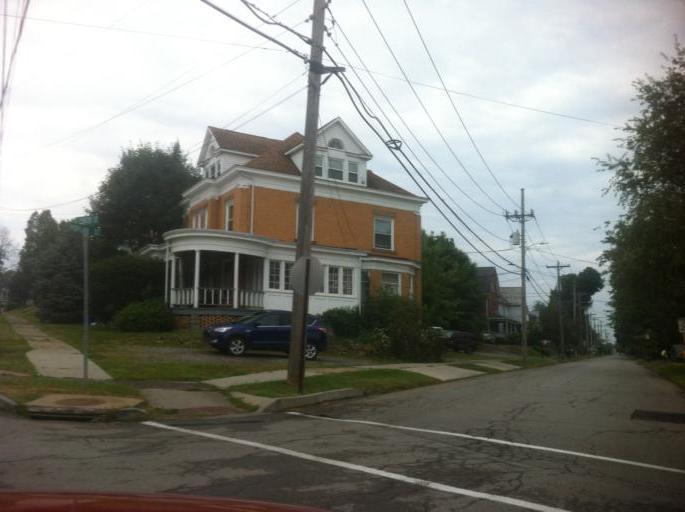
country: US
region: Pennsylvania
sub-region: Mercer County
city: Grove City
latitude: 41.1574
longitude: -80.0901
